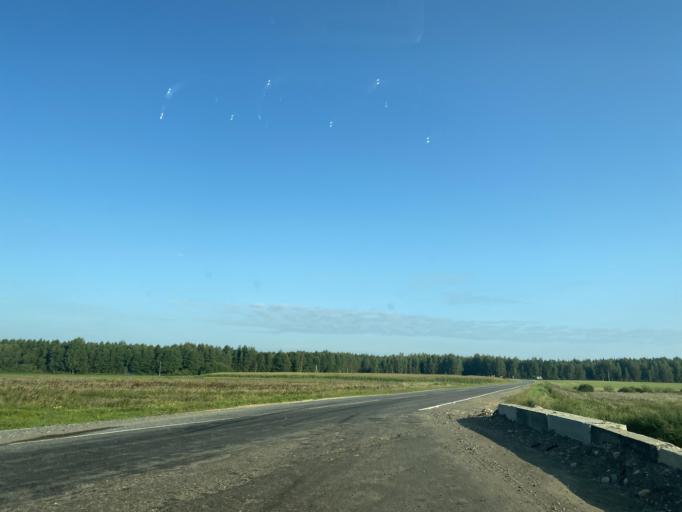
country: BY
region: Minsk
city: Loshnitsa
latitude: 54.0964
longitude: 28.6932
